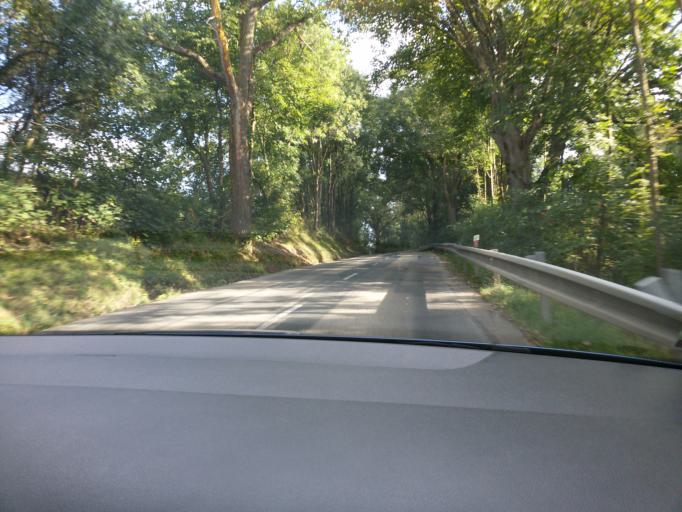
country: CZ
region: South Moravian
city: Olesnice
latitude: 49.5436
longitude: 16.4377
